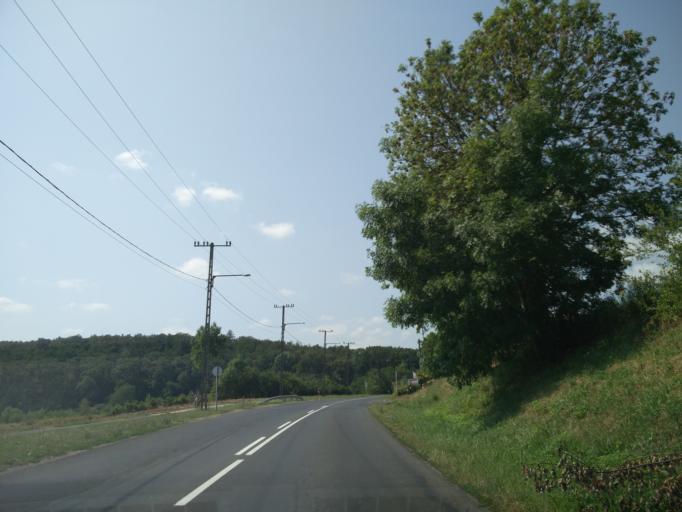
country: HU
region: Zala
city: Zalaegerszeg
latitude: 46.8207
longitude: 16.8281
